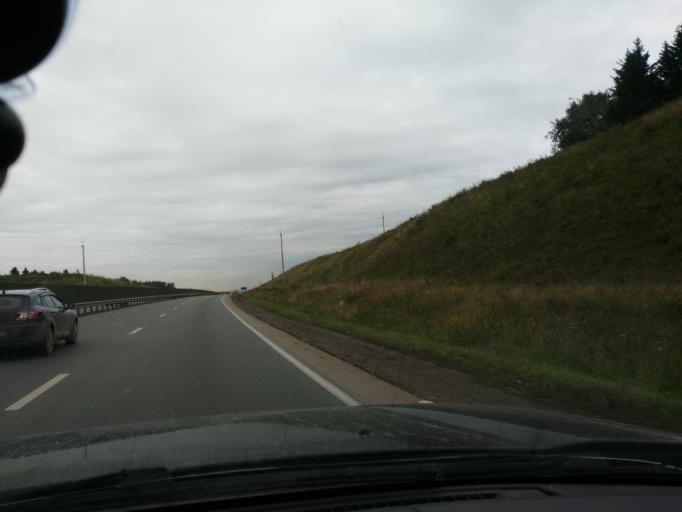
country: RU
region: Perm
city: Froly
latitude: 57.9350
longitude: 56.2186
